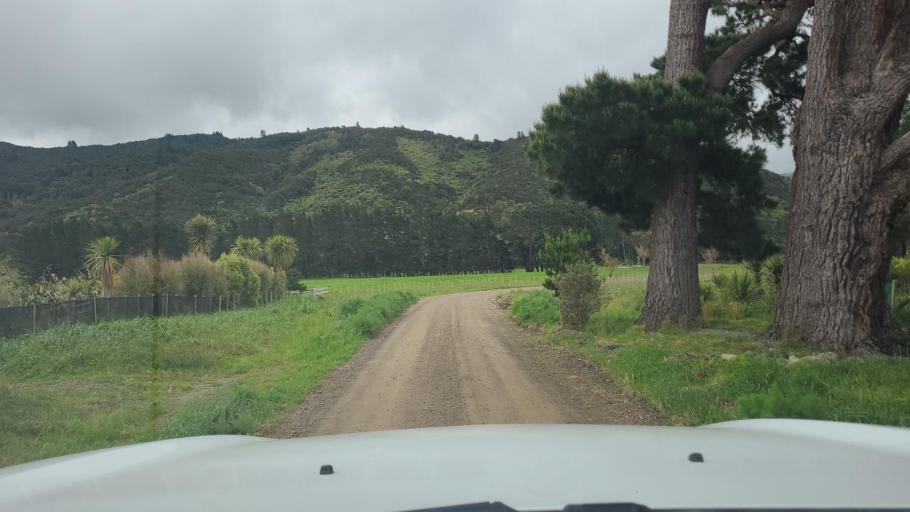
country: NZ
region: Wellington
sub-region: Upper Hutt City
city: Upper Hutt
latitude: -41.1199
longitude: 175.3129
